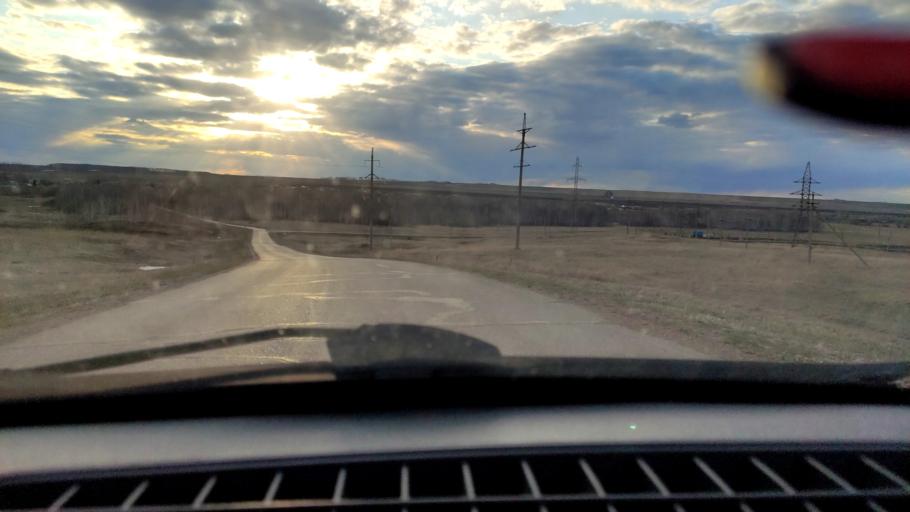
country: RU
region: Bashkortostan
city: Tolbazy
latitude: 54.0172
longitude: 55.7222
